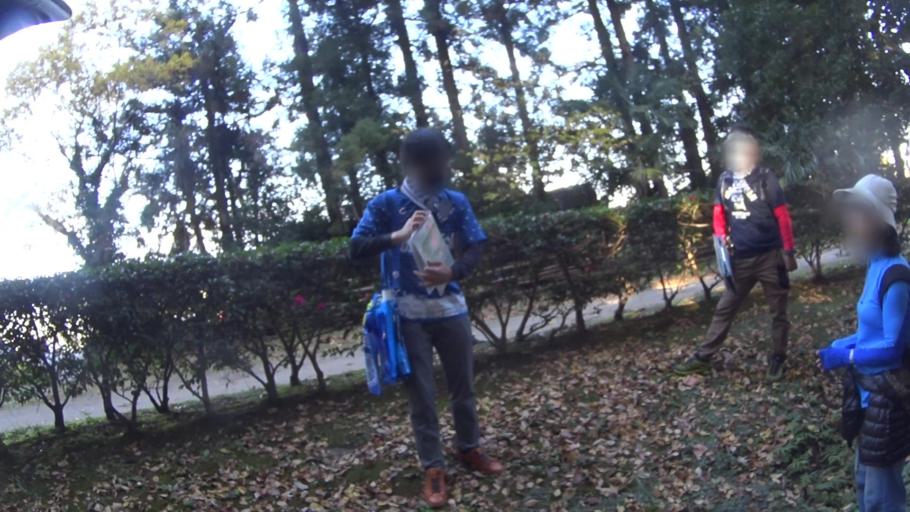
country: JP
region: Ibaraki
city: Mito-shi
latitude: 36.3799
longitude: 140.4736
